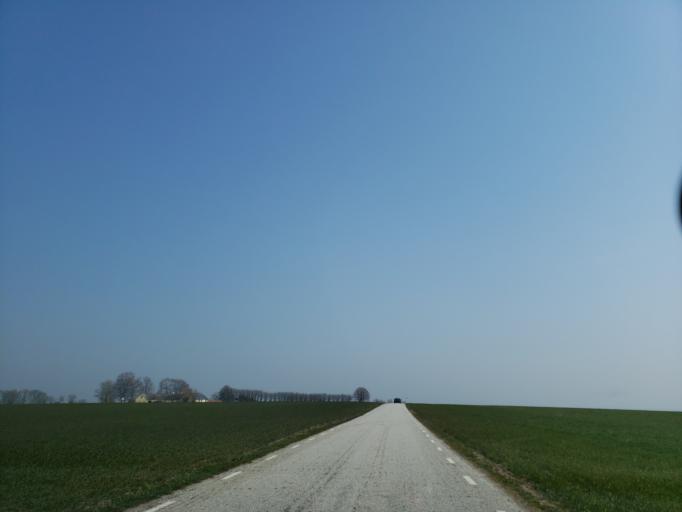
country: SE
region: Skane
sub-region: Simrishamns Kommun
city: Simrishamn
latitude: 55.5064
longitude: 14.3030
